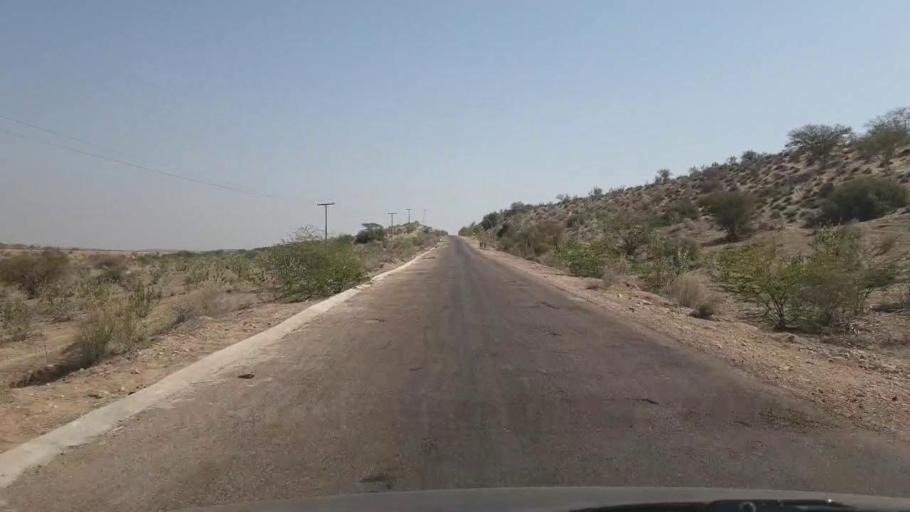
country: PK
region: Sindh
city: Chor
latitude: 25.5795
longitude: 69.9223
